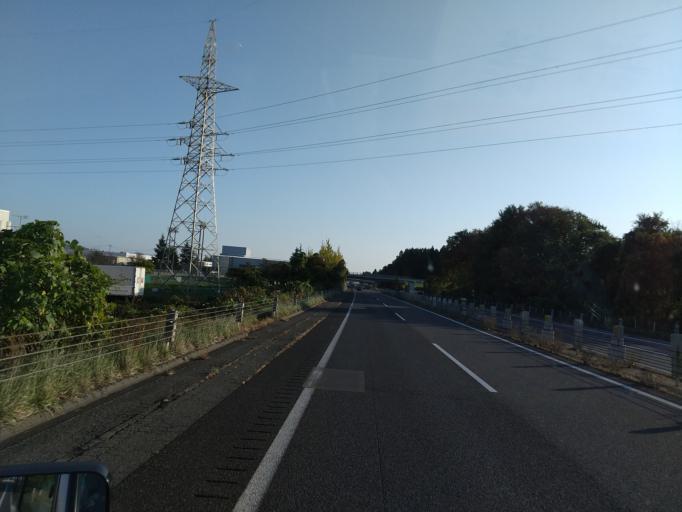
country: JP
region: Iwate
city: Kitakami
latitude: 39.3224
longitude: 141.0898
